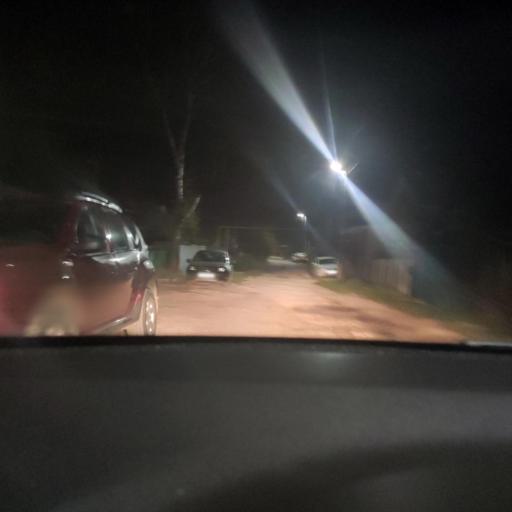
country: RU
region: Samara
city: Samara
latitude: 53.2227
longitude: 50.2221
